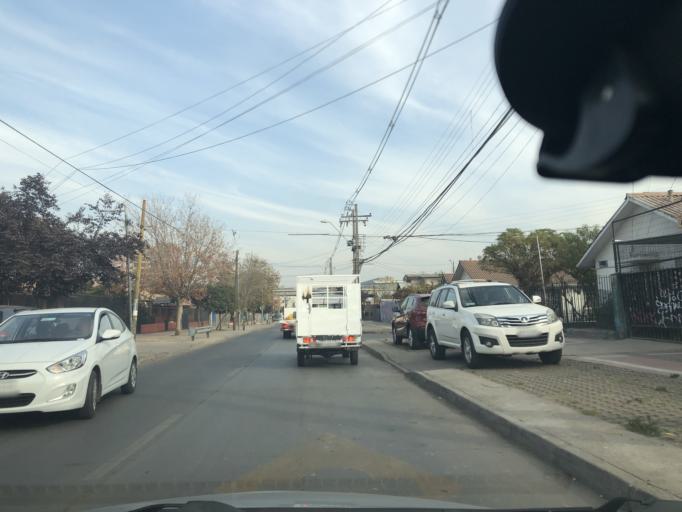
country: CL
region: Santiago Metropolitan
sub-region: Provincia de Cordillera
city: Puente Alto
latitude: -33.5860
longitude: -70.5784
